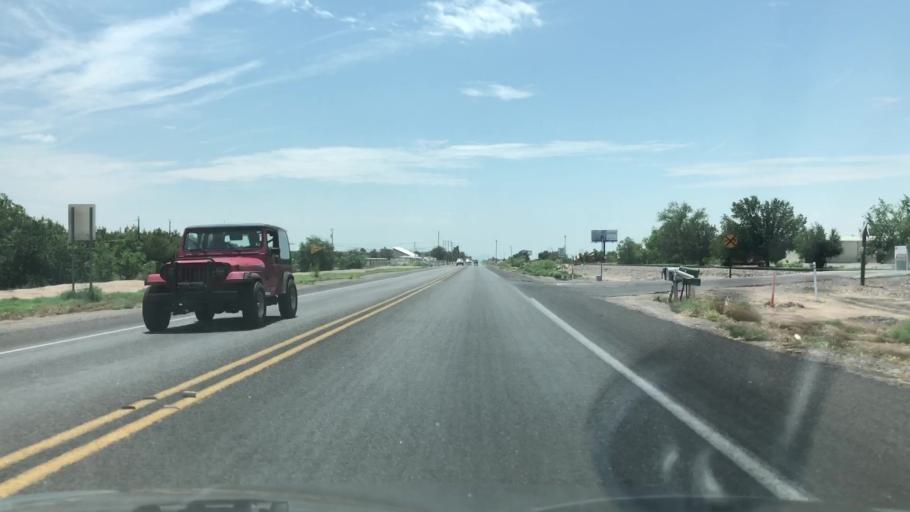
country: US
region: New Mexico
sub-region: Dona Ana County
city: University Park
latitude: 32.2576
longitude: -106.7554
